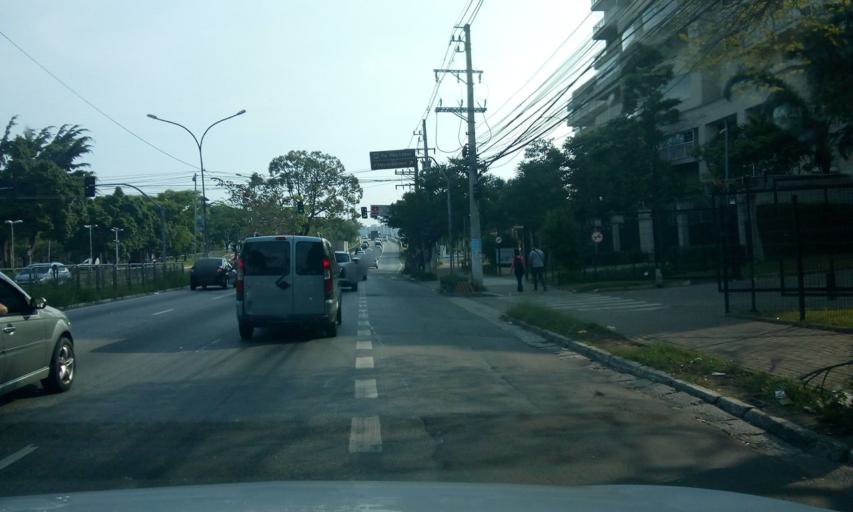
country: BR
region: Sao Paulo
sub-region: Osasco
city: Osasco
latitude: -23.5431
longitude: -46.7320
